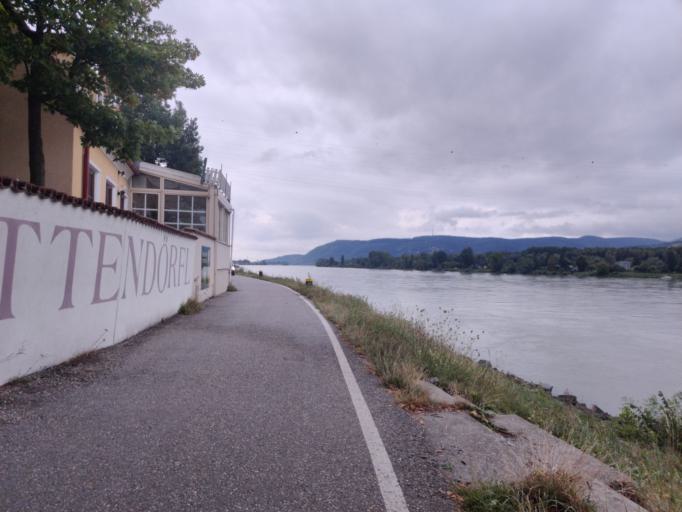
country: AT
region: Lower Austria
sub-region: Politischer Bezirk Korneuburg
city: Bisamberg
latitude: 48.3270
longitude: 16.3344
